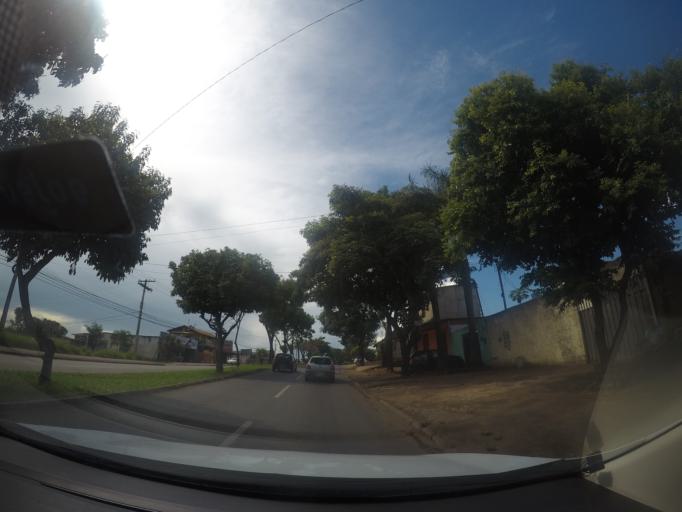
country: BR
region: Goias
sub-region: Trindade
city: Trindade
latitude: -16.6655
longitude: -49.3871
